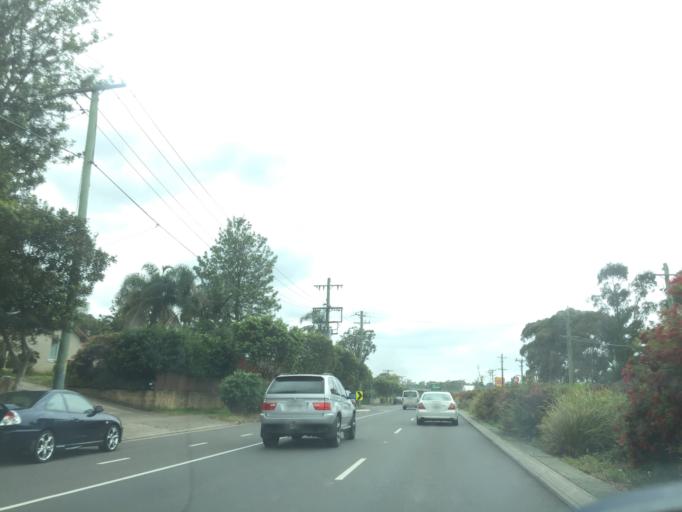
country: AU
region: New South Wales
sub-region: Holroyd
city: Girraween
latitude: -33.7668
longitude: 150.9527
